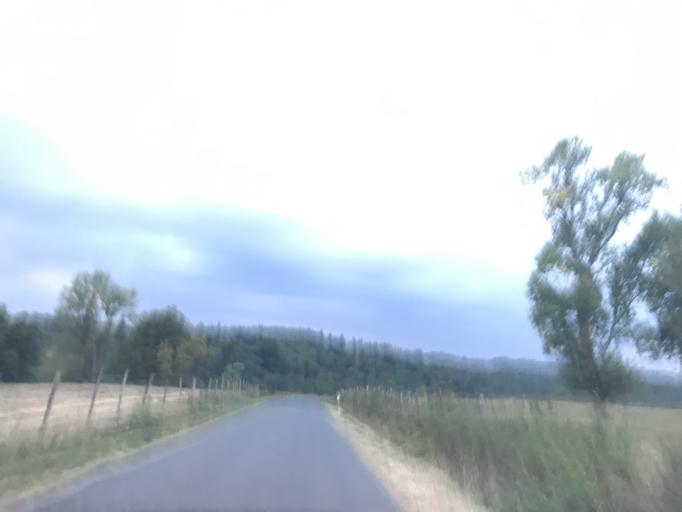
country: FR
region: Auvergne
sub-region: Departement du Puy-de-Dome
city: Escoutoux
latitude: 45.7898
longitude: 3.5765
